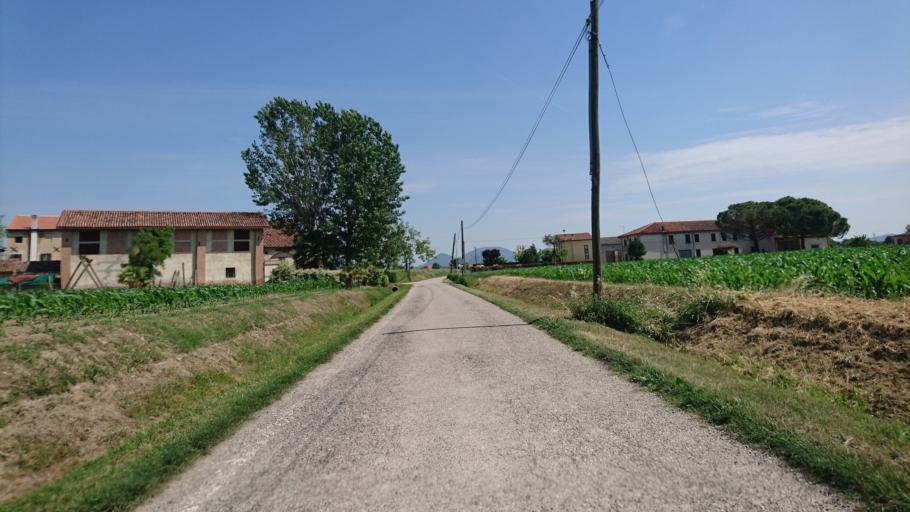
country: IT
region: Veneto
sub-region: Provincia di Padova
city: Ospedaletto Euganeo
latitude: 45.2068
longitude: 11.5927
